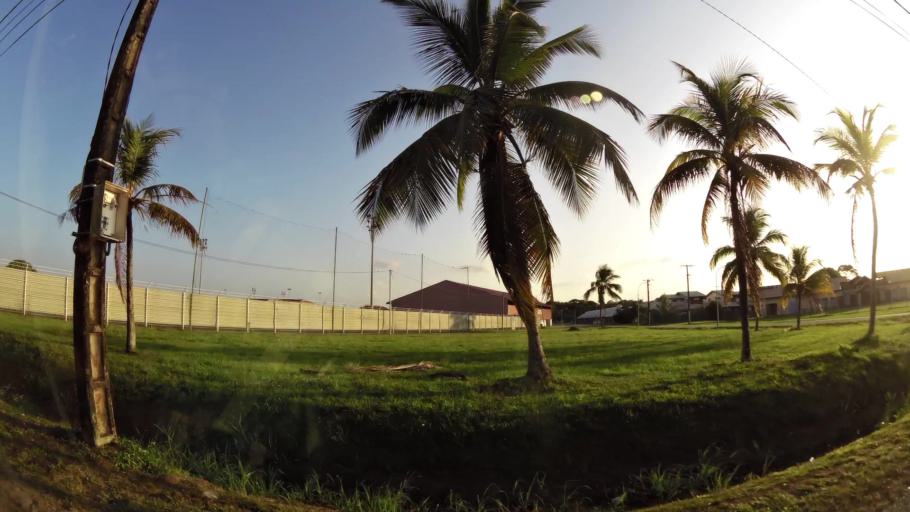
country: GF
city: Macouria
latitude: 5.0138
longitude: -52.4765
